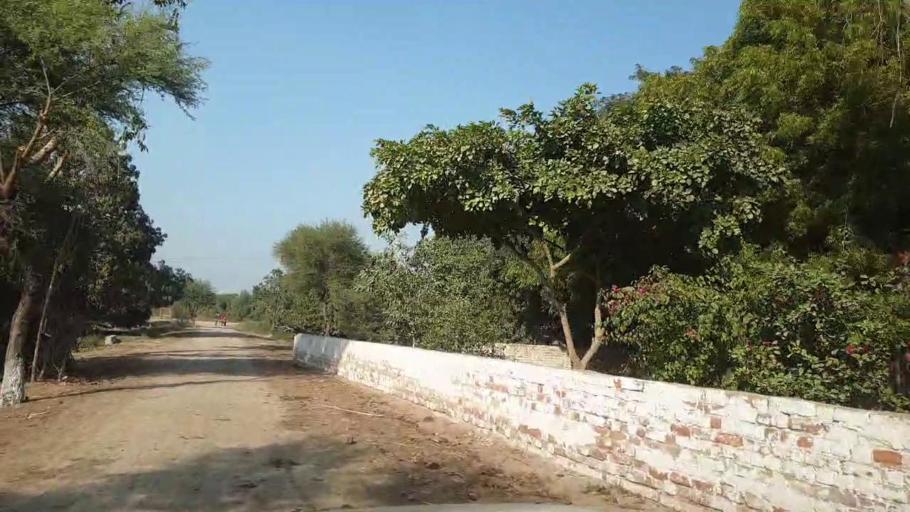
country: PK
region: Sindh
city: Tando Allahyar
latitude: 25.5679
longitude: 68.6720
